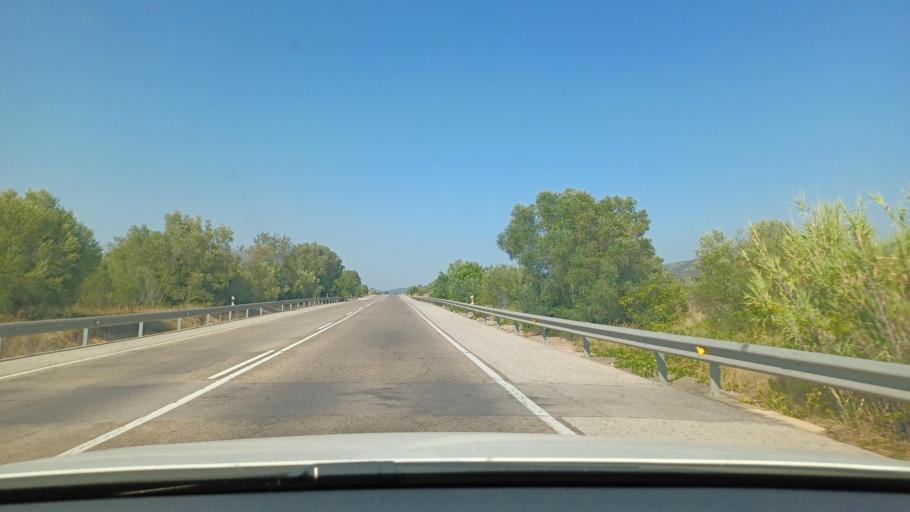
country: ES
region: Valencia
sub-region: Provincia de Castello
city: Alcala de Xivert
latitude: 40.3309
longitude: 0.2523
